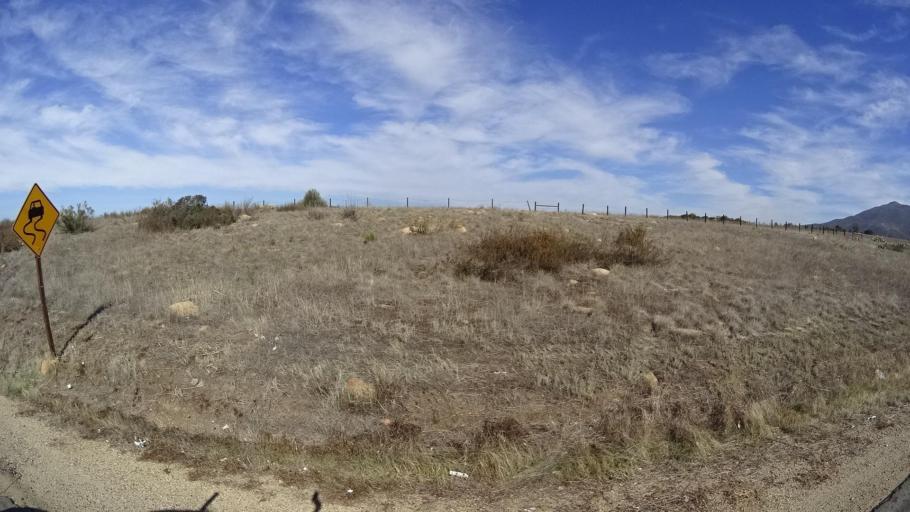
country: US
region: California
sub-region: San Diego County
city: Alpine
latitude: 32.8168
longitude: -116.7631
